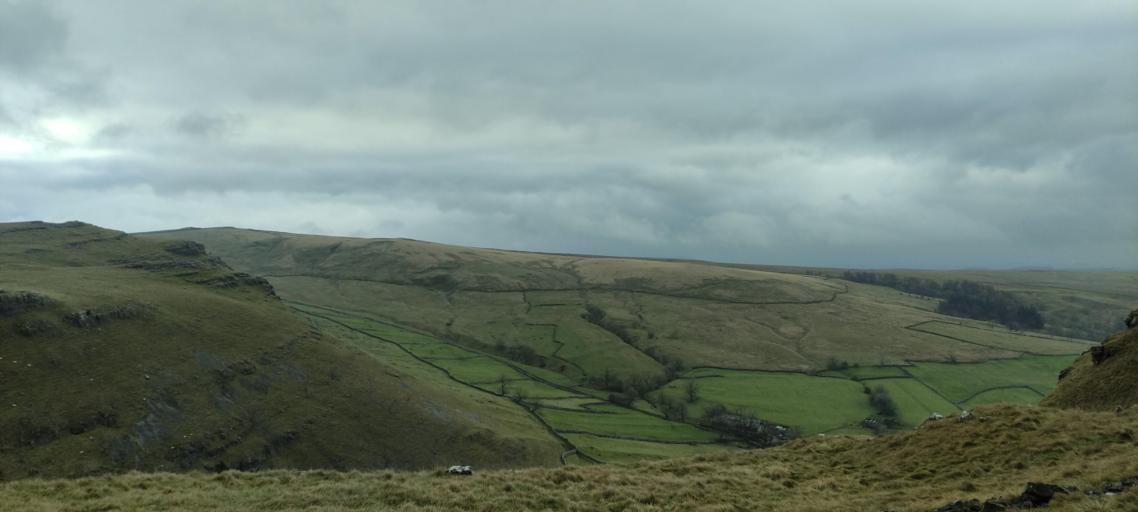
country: GB
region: England
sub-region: North Yorkshire
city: Gargrave
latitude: 54.0718
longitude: -2.1350
